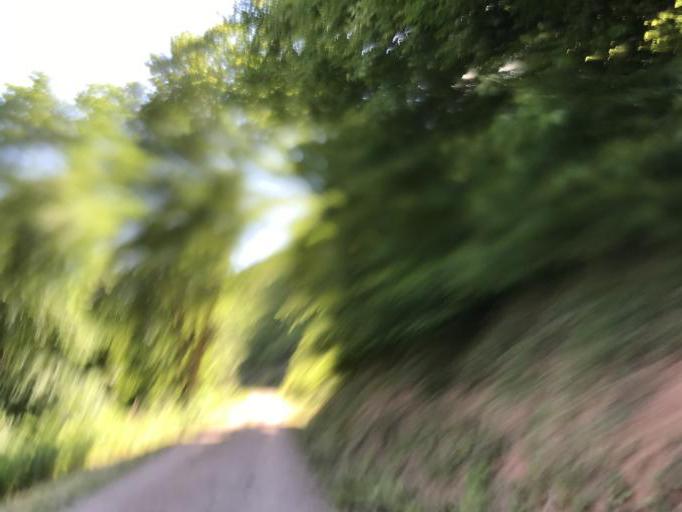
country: DE
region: Baden-Wuerttemberg
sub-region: Freiburg Region
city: Hausen
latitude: 47.6721
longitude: 7.8290
